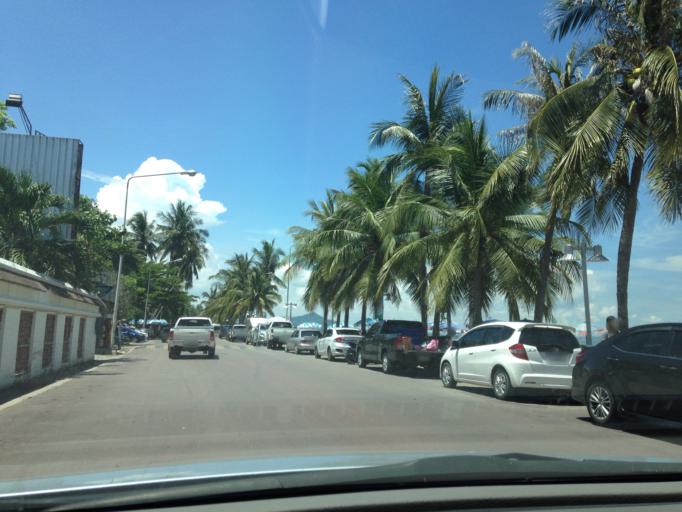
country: TH
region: Chon Buri
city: Si Racha
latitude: 13.2772
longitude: 100.9195
